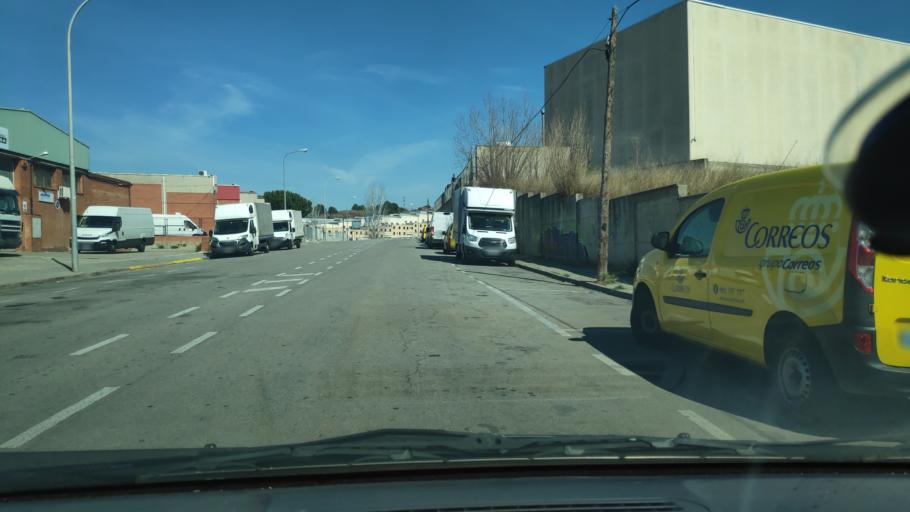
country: ES
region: Catalonia
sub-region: Provincia de Barcelona
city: Rubi
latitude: 41.5026
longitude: 2.0409
